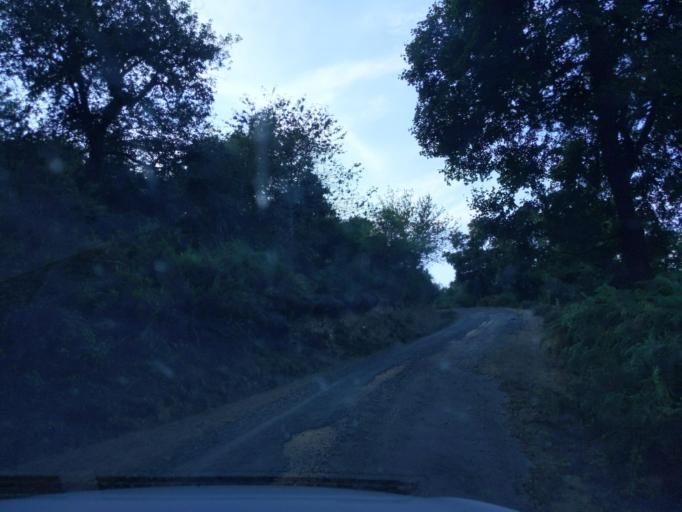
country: ES
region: La Rioja
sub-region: Provincia de La Rioja
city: Ojacastro
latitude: 42.3783
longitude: -3.0136
